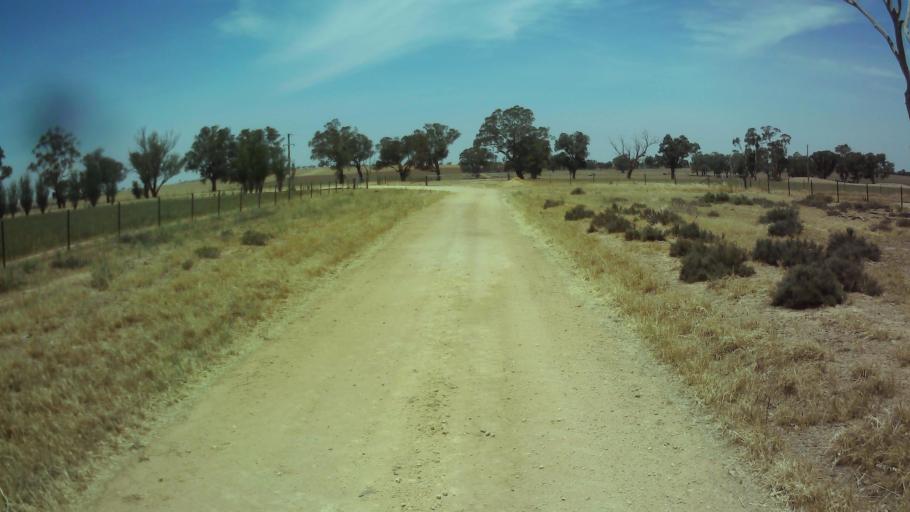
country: AU
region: New South Wales
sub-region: Weddin
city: Grenfell
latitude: -34.0044
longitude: 148.3973
